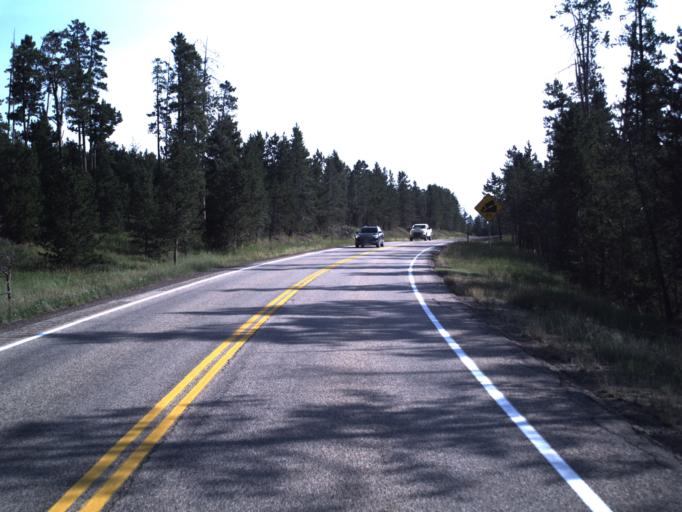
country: US
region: Utah
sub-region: Daggett County
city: Manila
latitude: 40.8468
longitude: -109.4651
